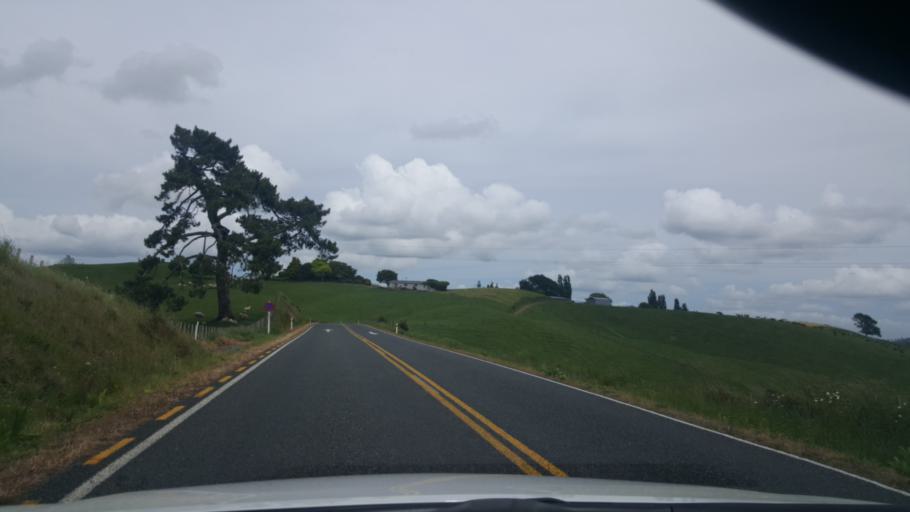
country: NZ
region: Waikato
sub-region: Matamata-Piako District
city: Matamata
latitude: -37.8745
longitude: 175.6856
